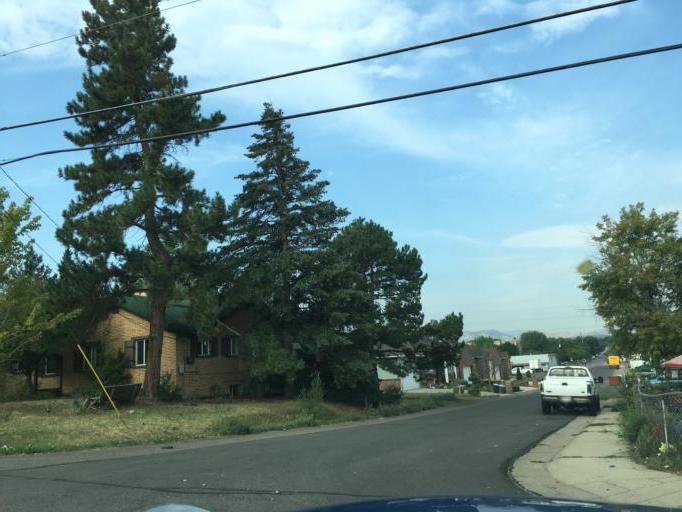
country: US
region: Colorado
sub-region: Jefferson County
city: Wheat Ridge
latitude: 39.7529
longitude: -105.1065
